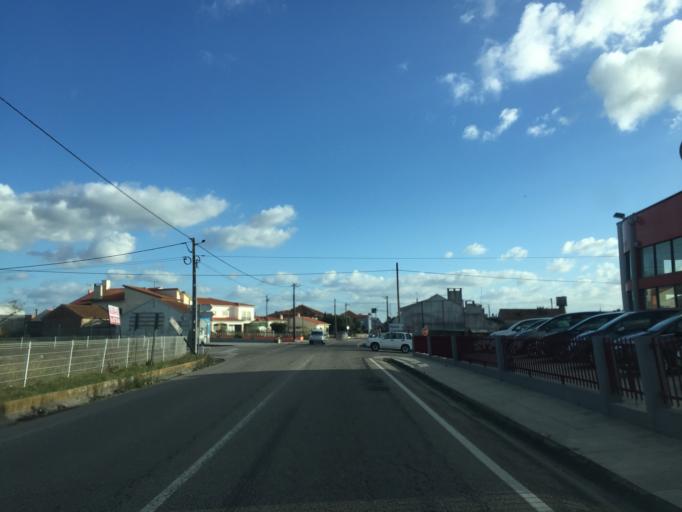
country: PT
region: Leiria
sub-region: Pombal
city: Lourical
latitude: 39.9851
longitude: -8.7998
